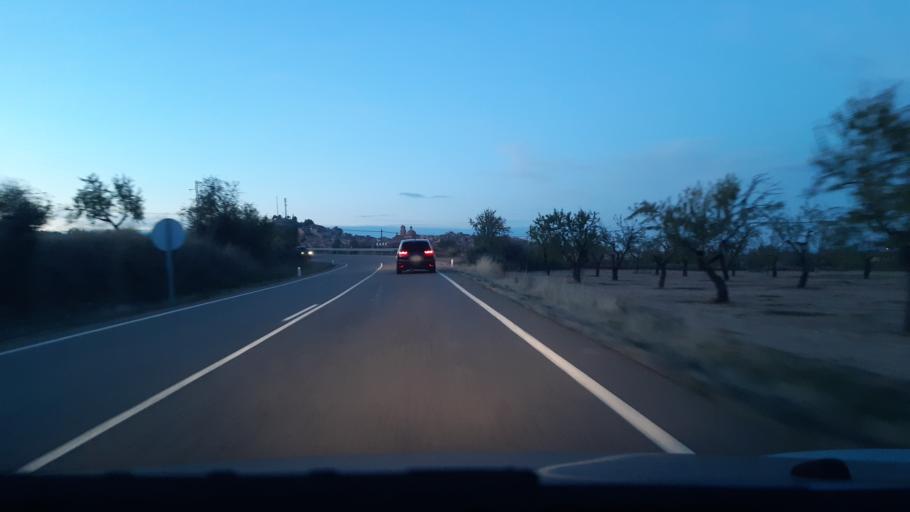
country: ES
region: Aragon
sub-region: Provincia de Teruel
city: Calaceite
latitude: 41.0084
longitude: 0.1908
